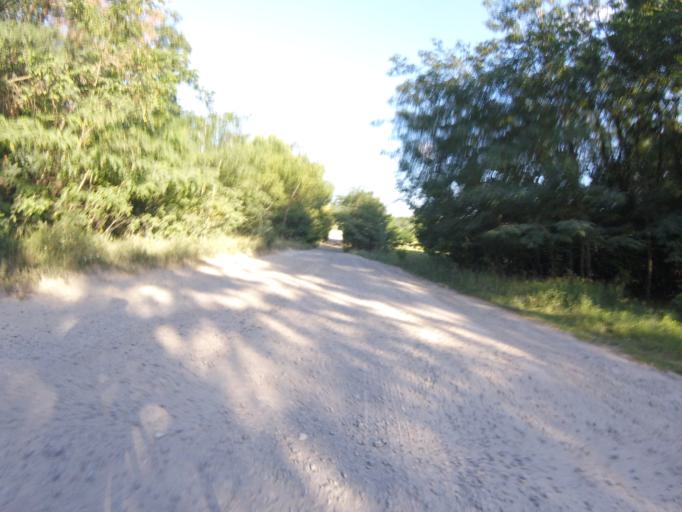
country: DE
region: Brandenburg
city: Zossen
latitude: 52.1986
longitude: 13.5051
